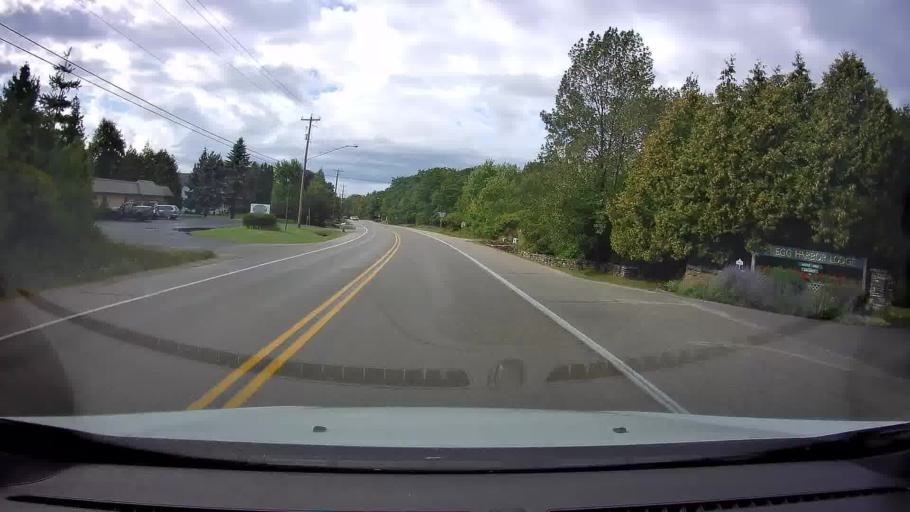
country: US
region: Wisconsin
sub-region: Door County
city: Sturgeon Bay
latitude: 45.0583
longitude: -87.2784
